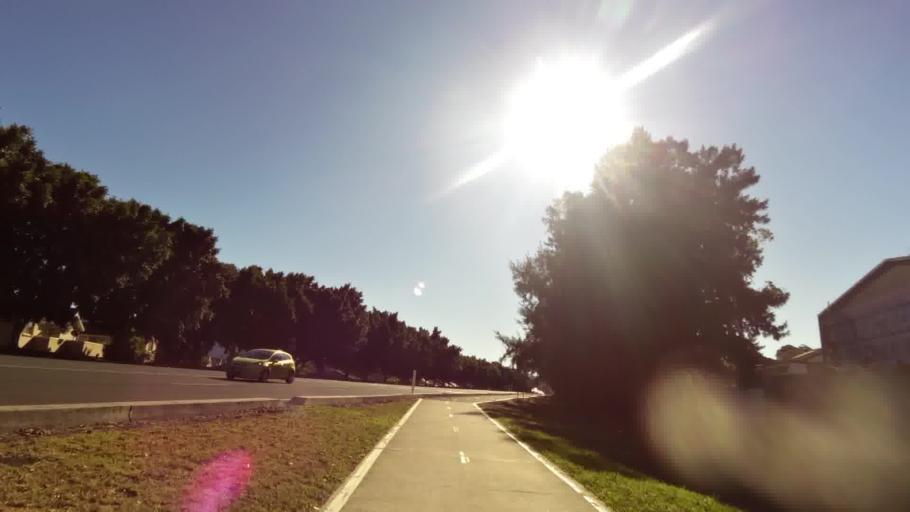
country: AU
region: New South Wales
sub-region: Wollongong
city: Koonawarra
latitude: -34.4889
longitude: 150.7976
